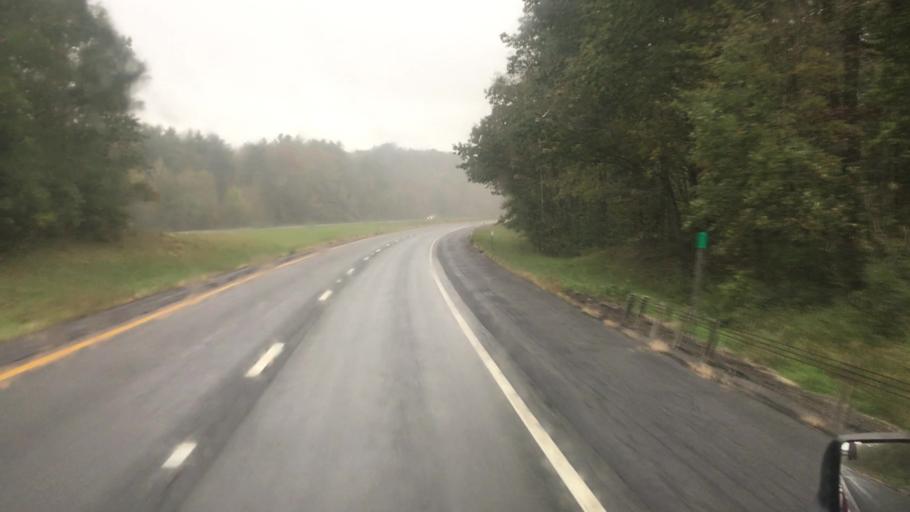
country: US
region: New York
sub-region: Chenango County
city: Bainbridge
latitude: 42.1877
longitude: -75.5880
